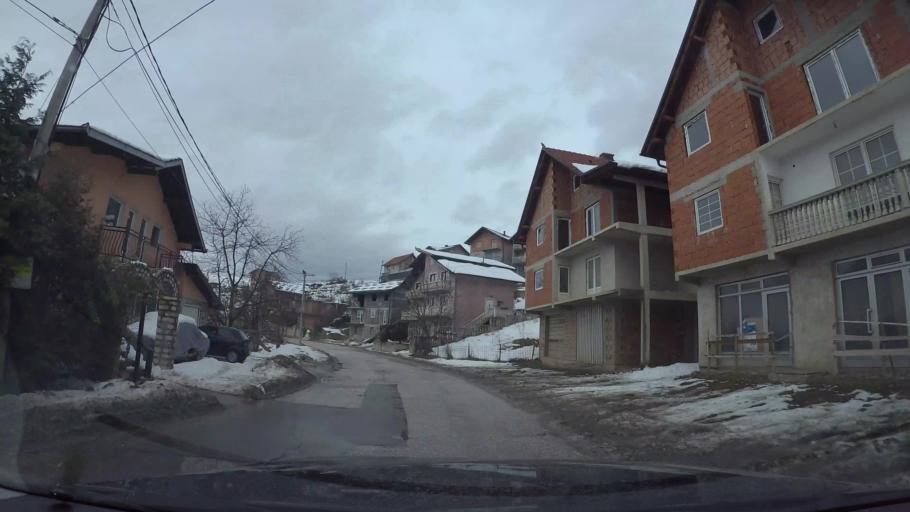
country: BA
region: Federation of Bosnia and Herzegovina
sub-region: Kanton Sarajevo
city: Sarajevo
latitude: 43.8638
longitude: 18.3508
